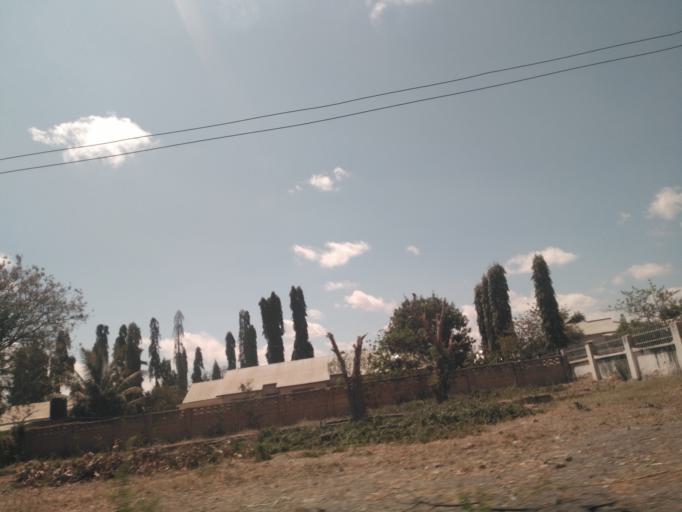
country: TZ
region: Dodoma
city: Dodoma
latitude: -6.1670
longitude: 35.7647
